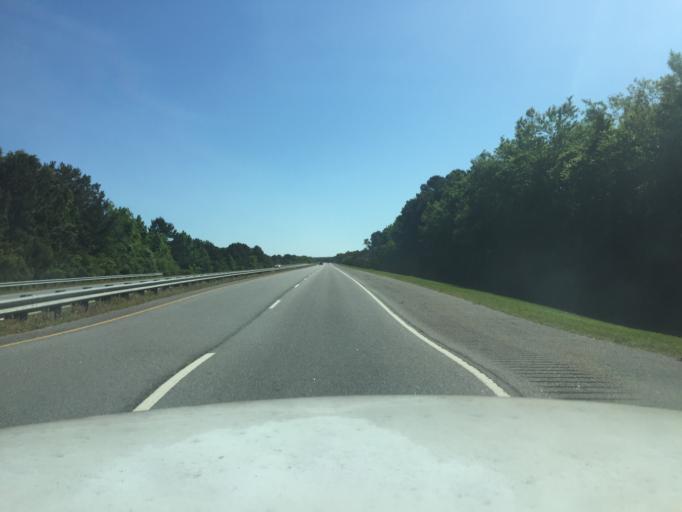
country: US
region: Georgia
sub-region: Chatham County
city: Georgetown
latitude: 32.0064
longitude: -81.1930
